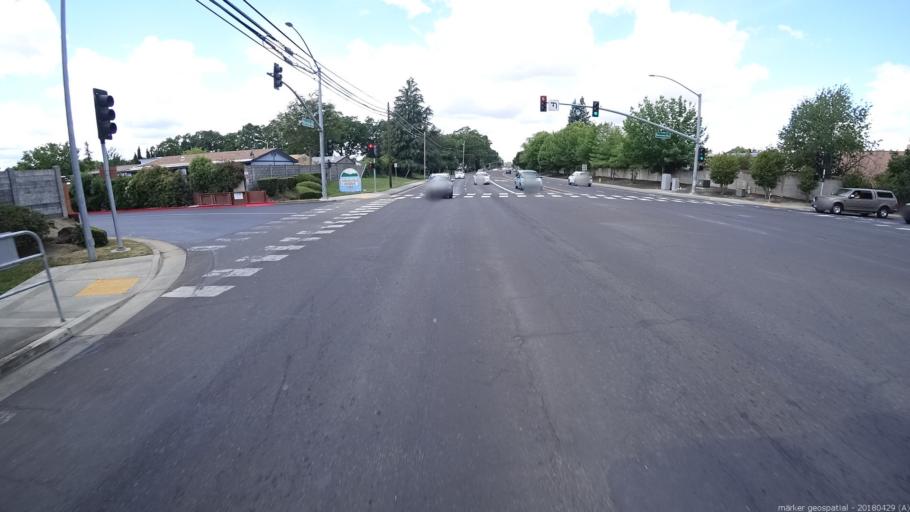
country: US
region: California
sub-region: Yolo County
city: West Sacramento
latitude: 38.5902
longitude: -121.5333
